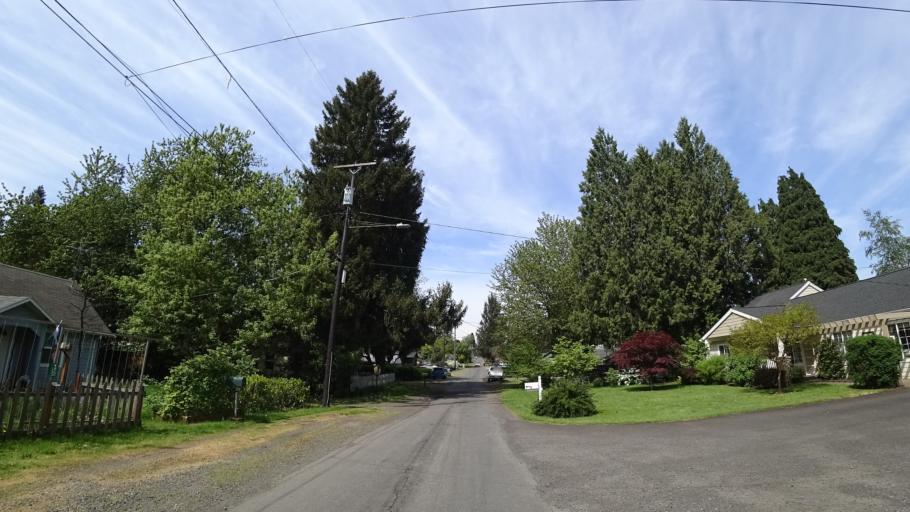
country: US
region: Oregon
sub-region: Clackamas County
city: Milwaukie
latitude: 45.4459
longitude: -122.6124
